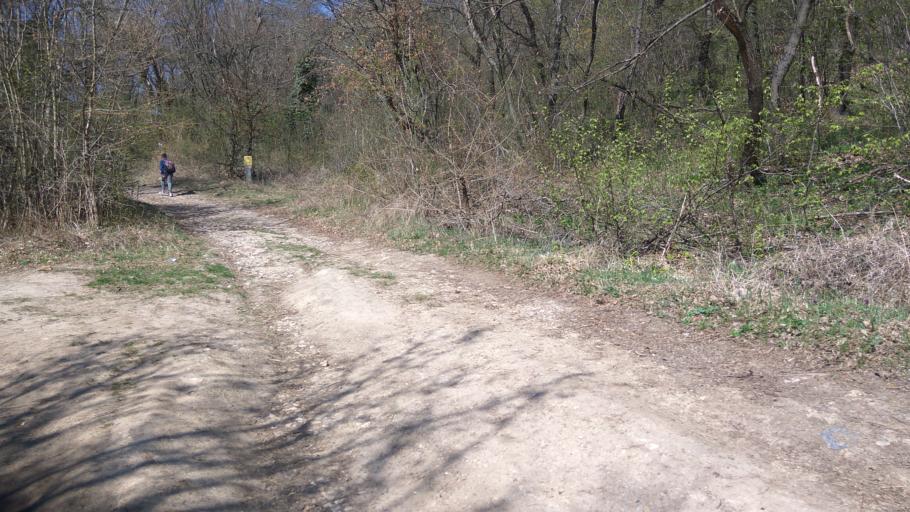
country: HU
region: Pest
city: Budaors
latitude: 47.4872
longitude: 18.9762
